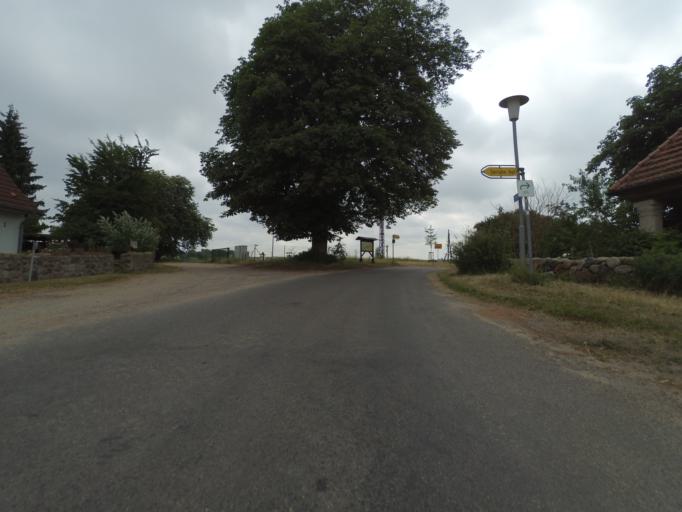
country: DE
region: Mecklenburg-Vorpommern
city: Krakow am See
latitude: 53.6655
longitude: 12.3488
